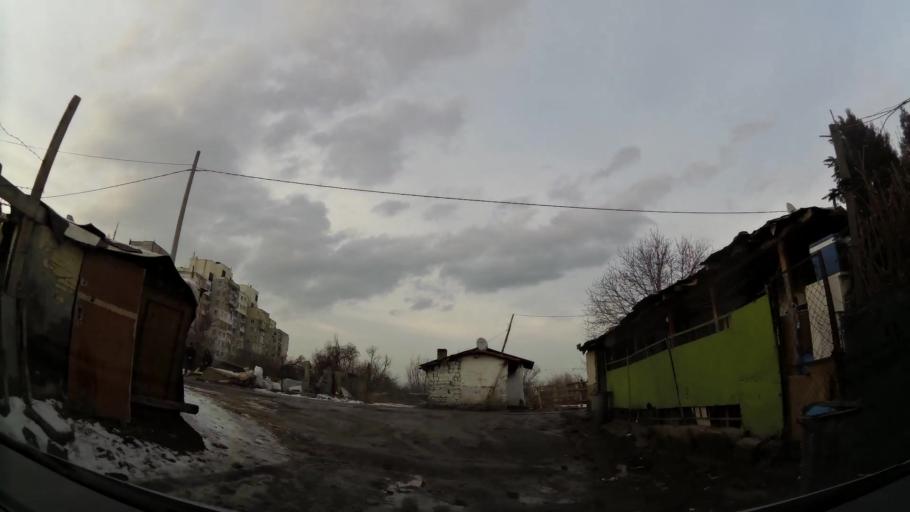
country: BG
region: Sofia-Capital
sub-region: Stolichna Obshtina
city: Sofia
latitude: 42.7264
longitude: 23.3469
